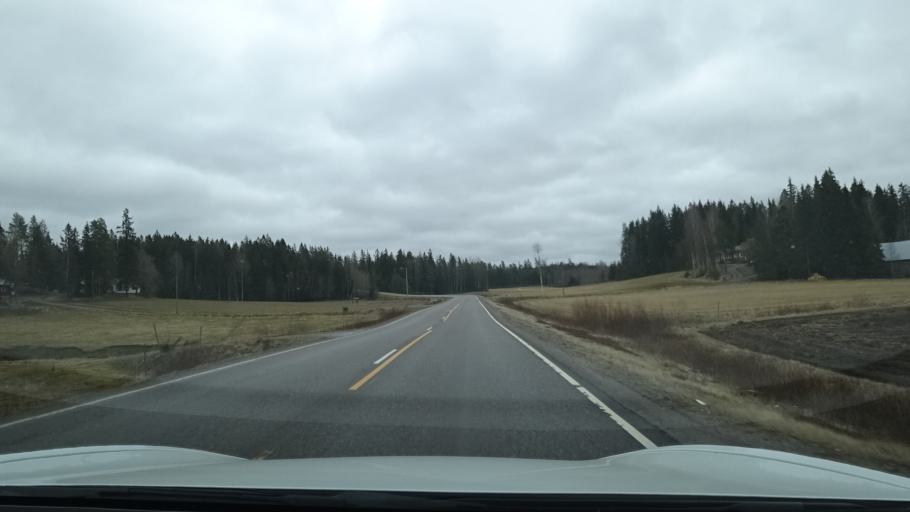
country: FI
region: Uusimaa
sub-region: Helsinki
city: Pornainen
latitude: 60.4844
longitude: 25.3949
